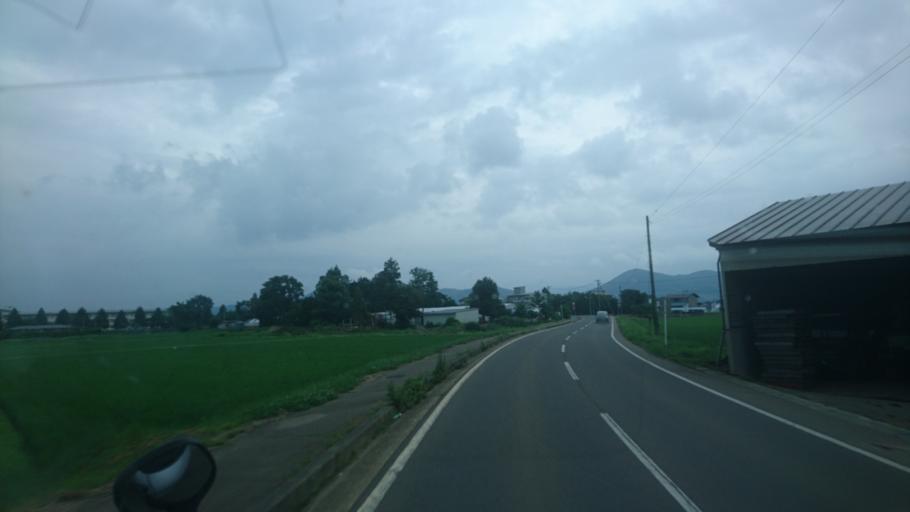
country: JP
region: Iwate
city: Morioka-shi
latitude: 39.6380
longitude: 141.1553
